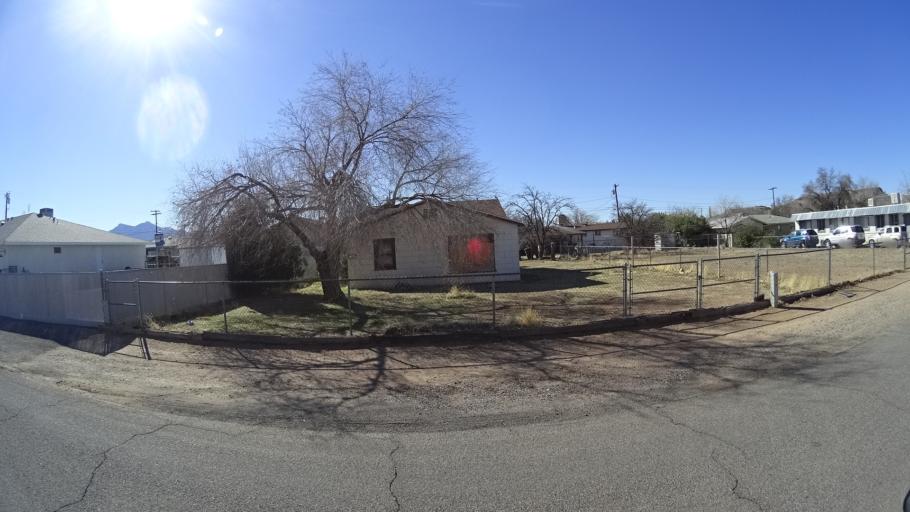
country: US
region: Arizona
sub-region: Mohave County
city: Kingman
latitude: 35.2053
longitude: -114.0276
